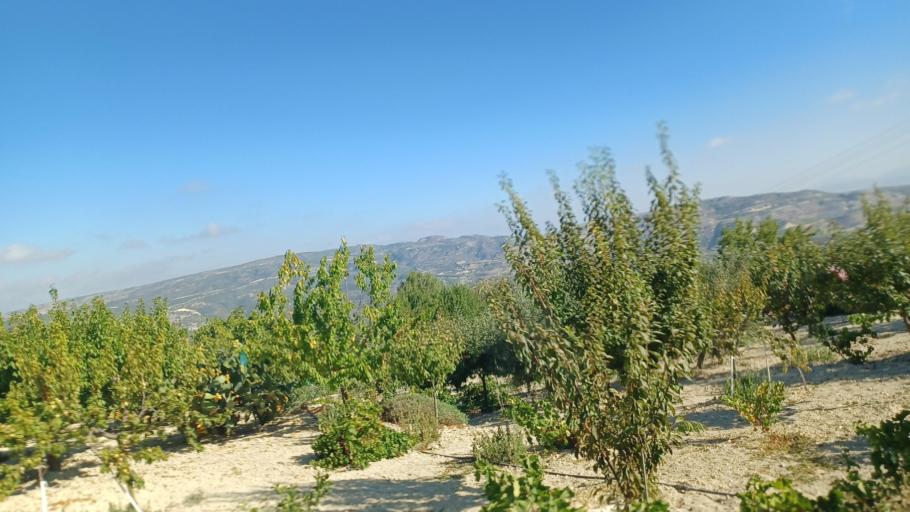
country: CY
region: Pafos
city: Tala
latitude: 34.8589
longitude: 32.4585
